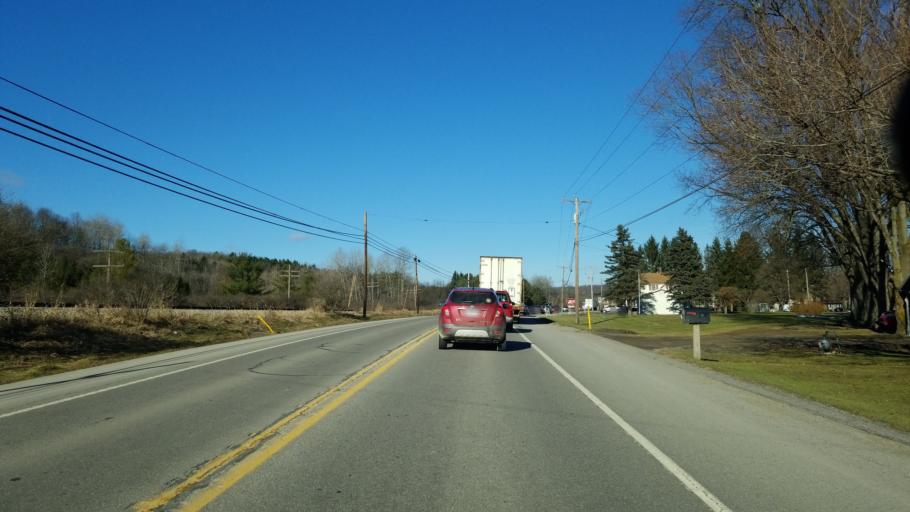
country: US
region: Pennsylvania
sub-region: Jefferson County
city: Brockway
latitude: 41.2283
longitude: -78.7817
